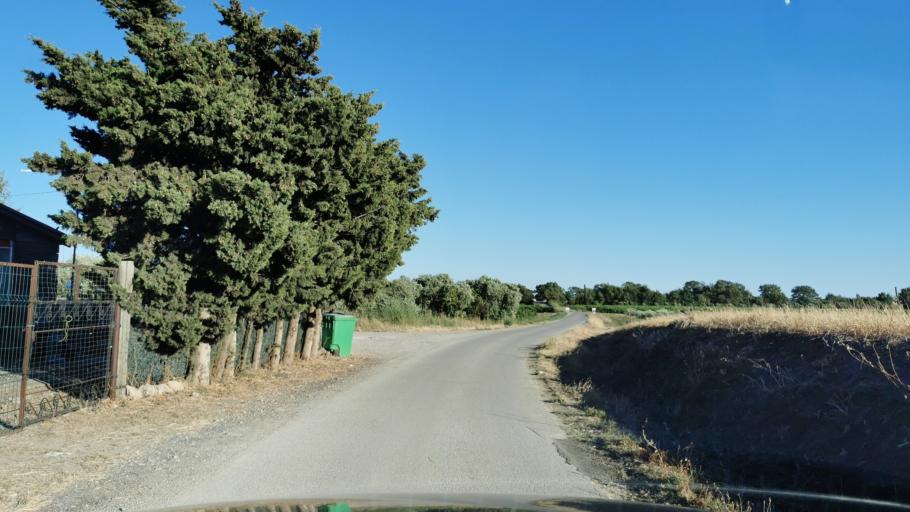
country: FR
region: Languedoc-Roussillon
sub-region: Departement de l'Aude
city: Ouveillan
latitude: 43.2643
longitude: 2.9845
